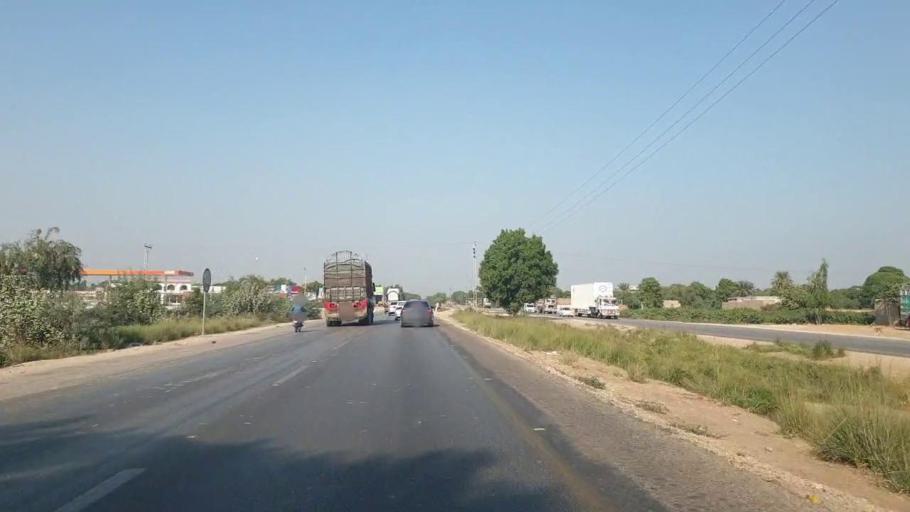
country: PK
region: Sindh
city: Matiari
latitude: 25.4973
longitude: 68.4240
